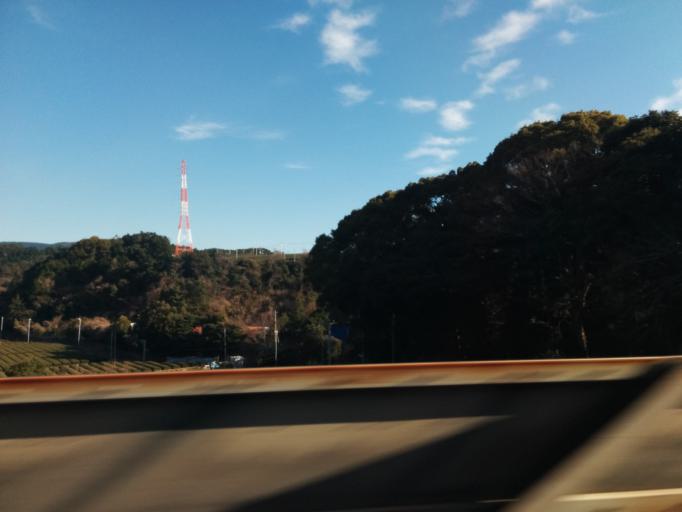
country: JP
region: Shizuoka
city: Numazu
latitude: 35.1374
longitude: 138.8176
